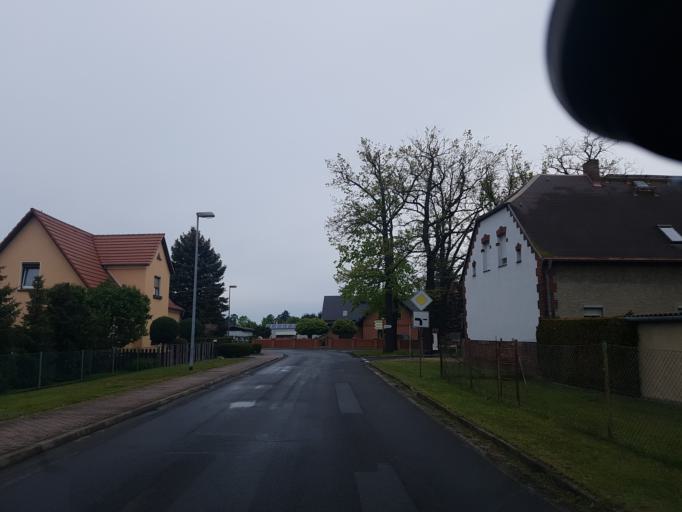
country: DE
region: Brandenburg
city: Spremberg
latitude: 51.6444
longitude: 14.4324
